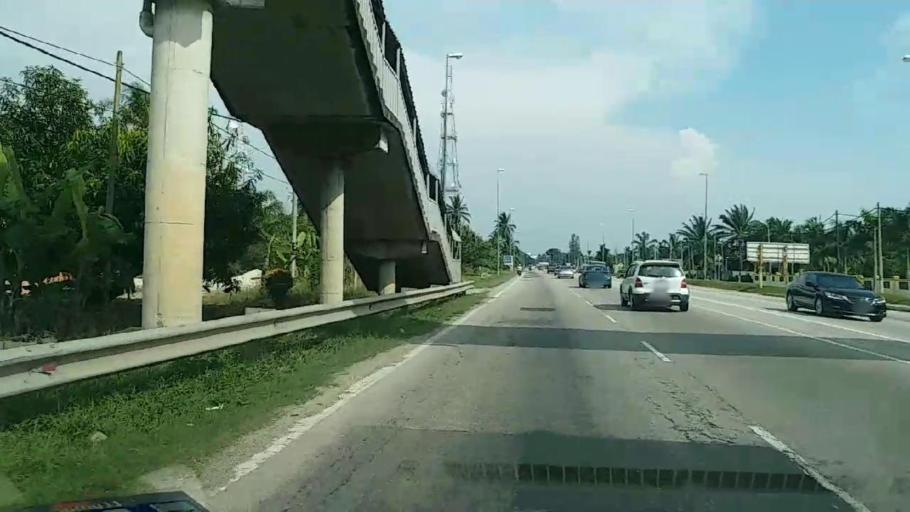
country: MY
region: Selangor
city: Kuala Selangor
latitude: 3.3624
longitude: 101.2476
